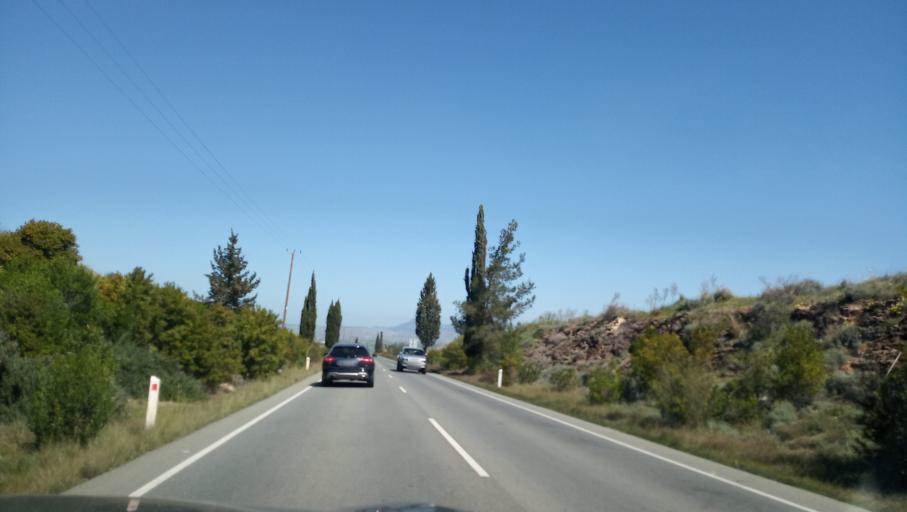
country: CY
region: Lefkosia
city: Astromeritis
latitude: 35.1197
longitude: 33.0087
